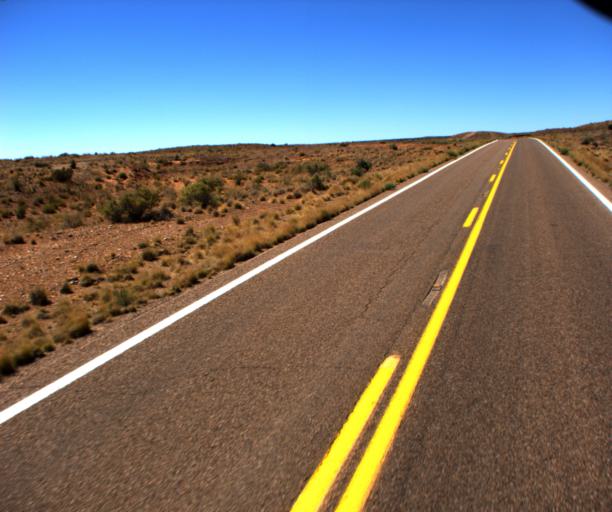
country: US
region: Arizona
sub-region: Navajo County
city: Winslow
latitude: 34.9616
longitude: -110.6473
